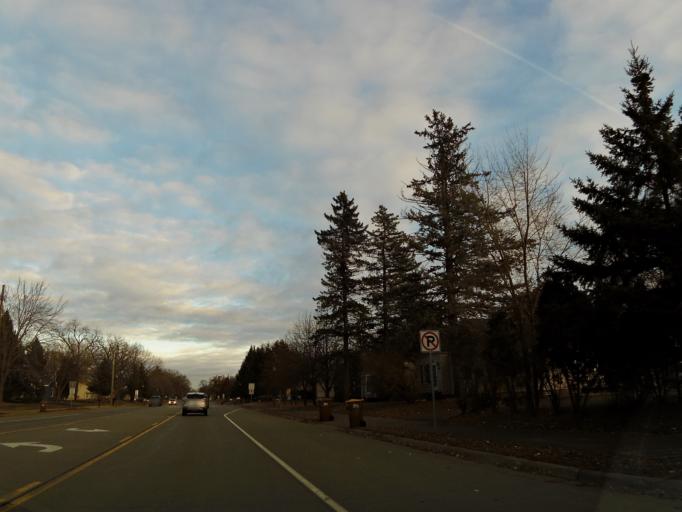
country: US
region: Minnesota
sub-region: Ramsey County
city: White Bear Lake
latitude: 45.0792
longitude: -93.0233
